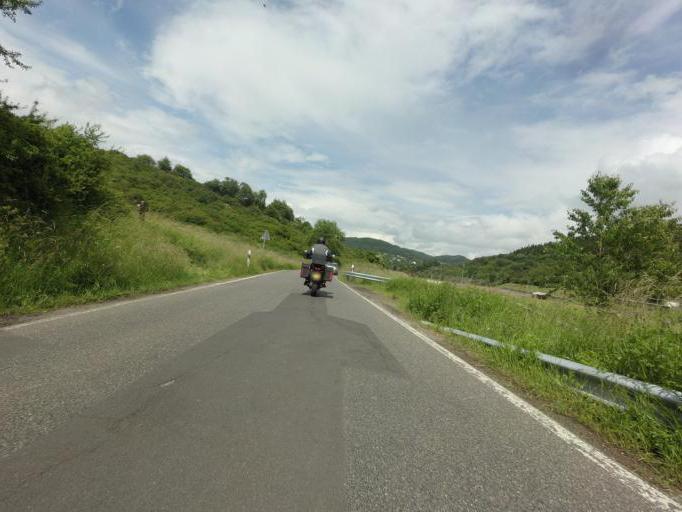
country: DE
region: Rheinland-Pfalz
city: Wimbach
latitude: 50.3737
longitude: 6.9218
